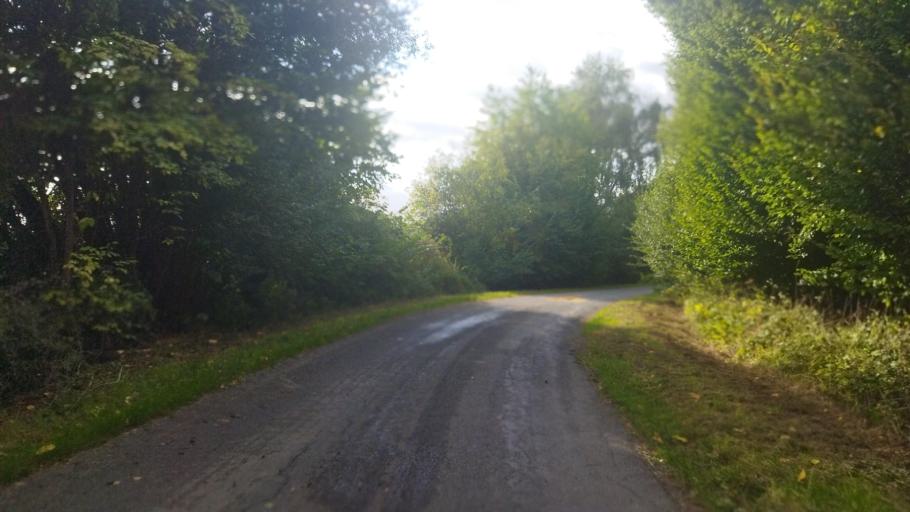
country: DE
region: North Rhine-Westphalia
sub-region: Regierungsbezirk Munster
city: Dulmen
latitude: 51.8768
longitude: 7.2617
